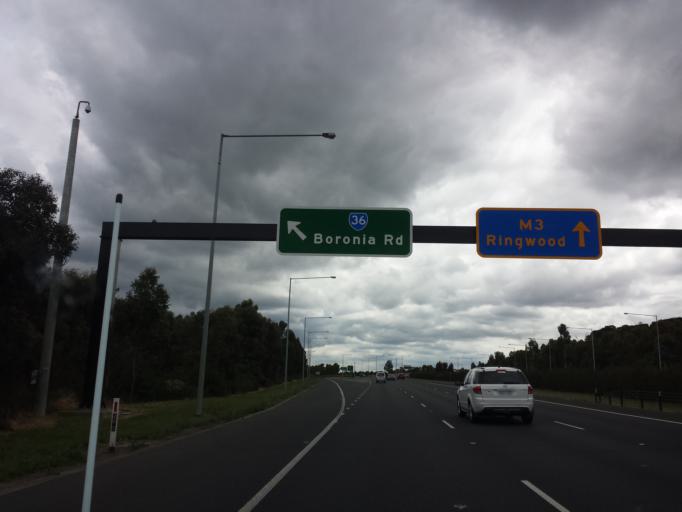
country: AU
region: Victoria
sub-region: Knox
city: Wantirna
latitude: -37.8514
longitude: 145.2153
